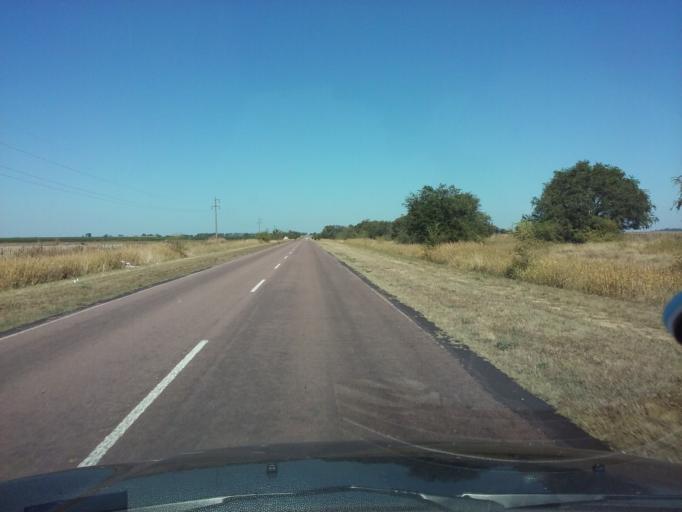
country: AR
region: La Pampa
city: Colonia Baron
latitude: -36.2564
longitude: -63.9429
